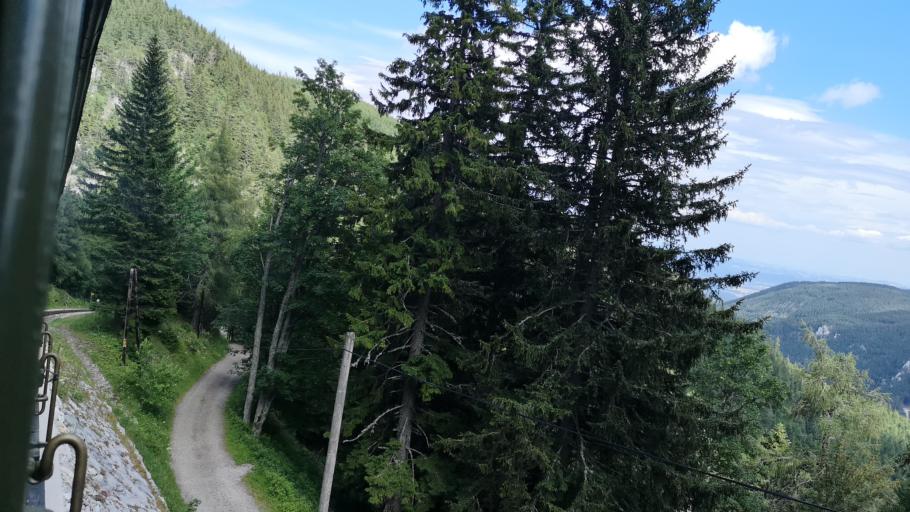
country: AT
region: Lower Austria
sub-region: Politischer Bezirk Neunkirchen
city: Reichenau an der Rax
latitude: 47.7535
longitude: 15.8545
